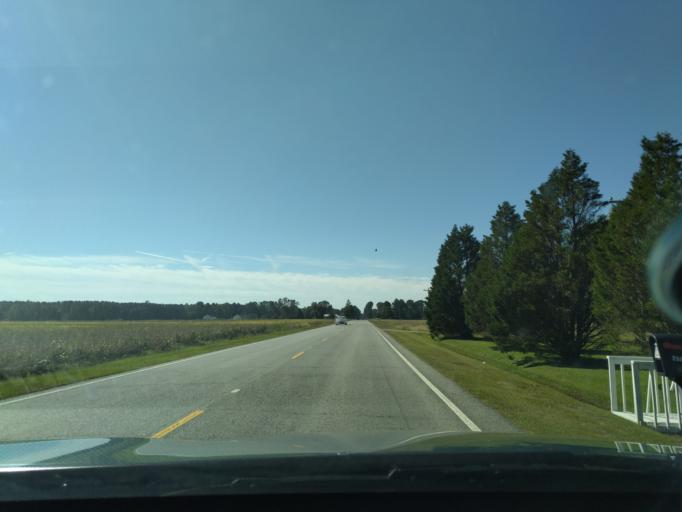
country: US
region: North Carolina
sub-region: Washington County
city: Plymouth
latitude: 35.7015
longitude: -76.7660
